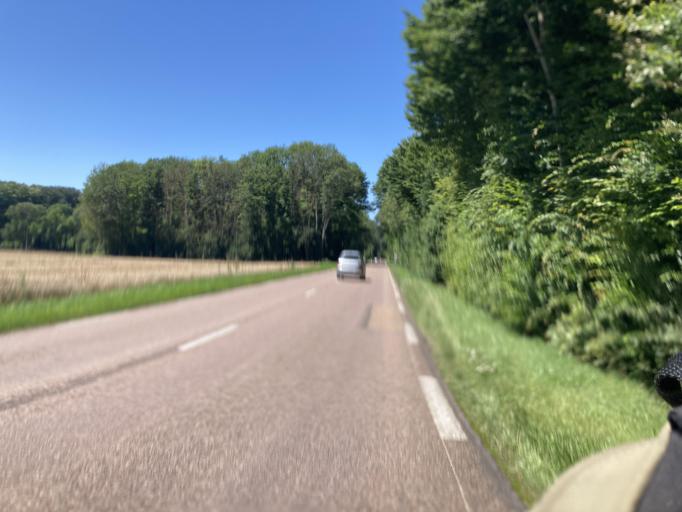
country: FR
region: Bourgogne
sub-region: Departement de l'Yonne
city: Laroche-Saint-Cydroine
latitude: 47.9654
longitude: 3.4665
